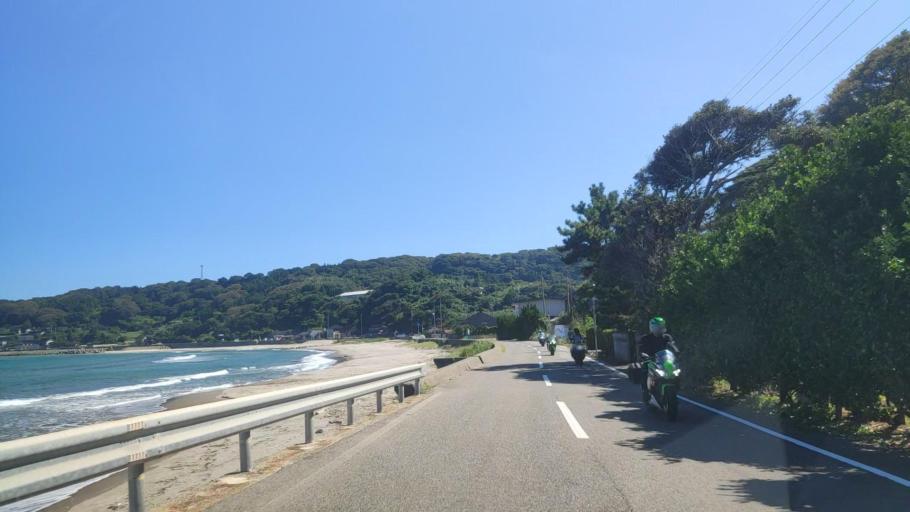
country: JP
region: Ishikawa
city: Nanao
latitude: 37.5284
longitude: 137.2788
